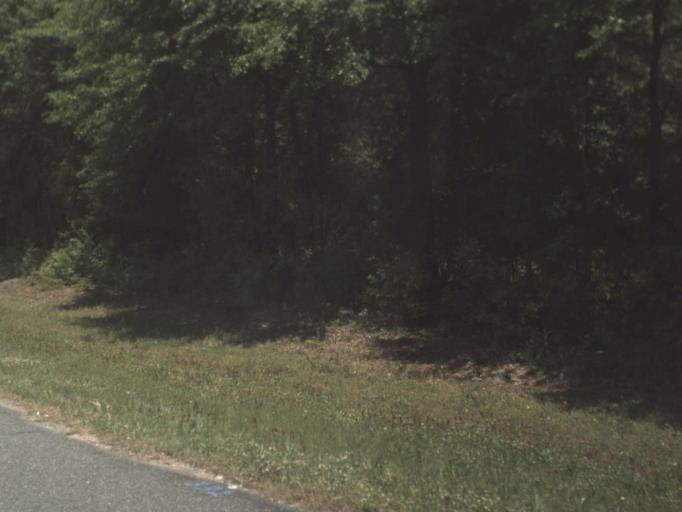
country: US
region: Florida
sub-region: Santa Rosa County
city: Point Baker
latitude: 30.7789
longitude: -87.0417
